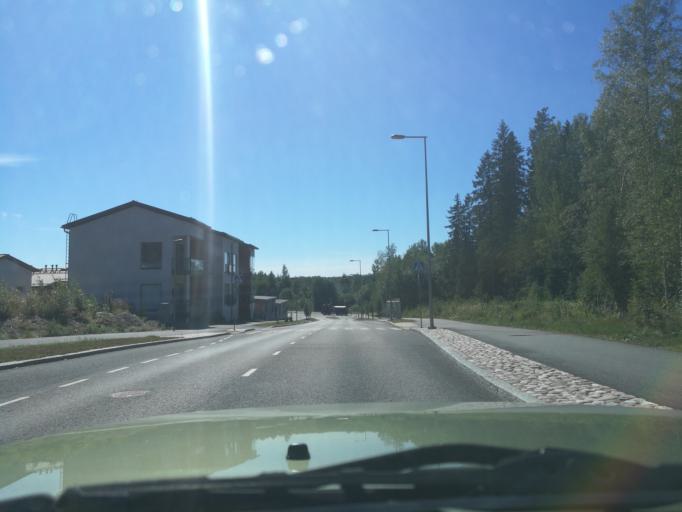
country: FI
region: Uusimaa
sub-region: Helsinki
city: Kerava
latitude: 60.3507
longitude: 25.1325
